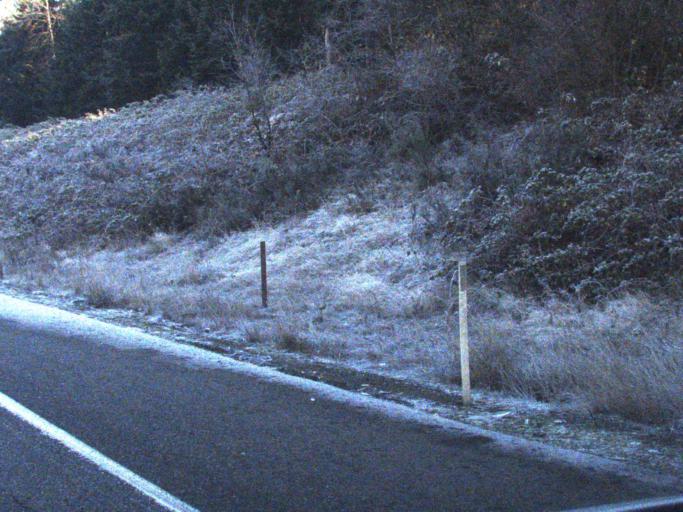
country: US
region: Washington
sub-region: King County
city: Lakeland South
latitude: 47.2845
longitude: -122.3081
